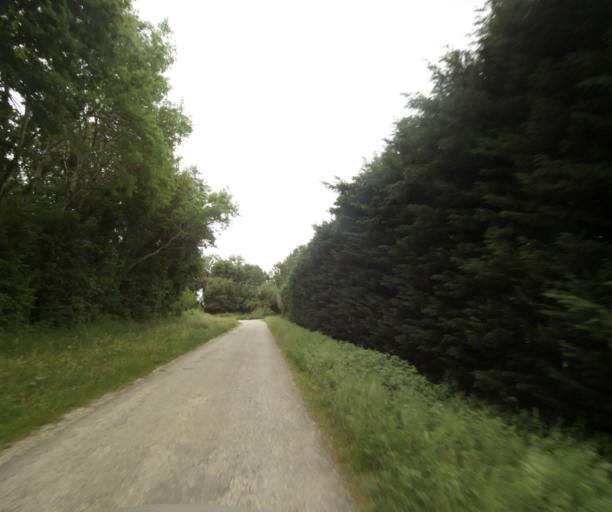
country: FR
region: Rhone-Alpes
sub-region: Departement de l'Ain
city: Mionnay
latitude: 45.8708
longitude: 4.9307
